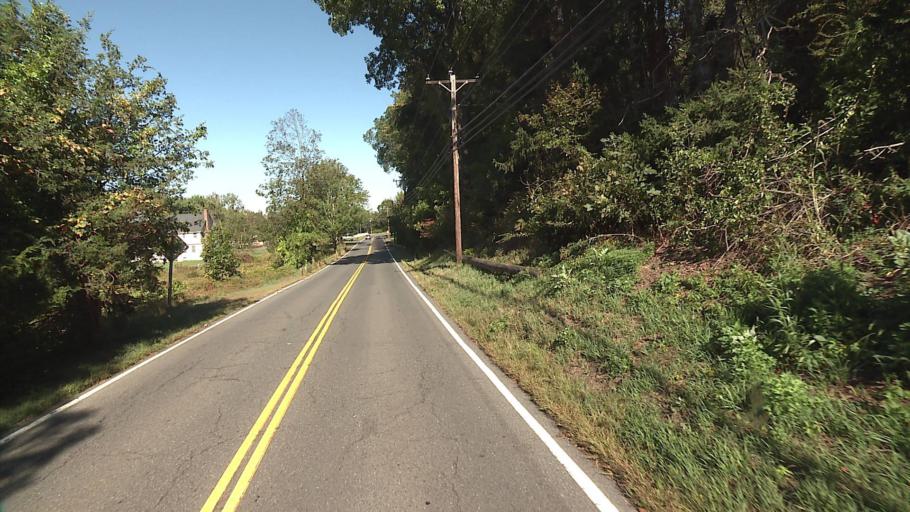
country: US
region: Connecticut
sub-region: Tolland County
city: Somers
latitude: 41.9682
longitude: -72.4418
